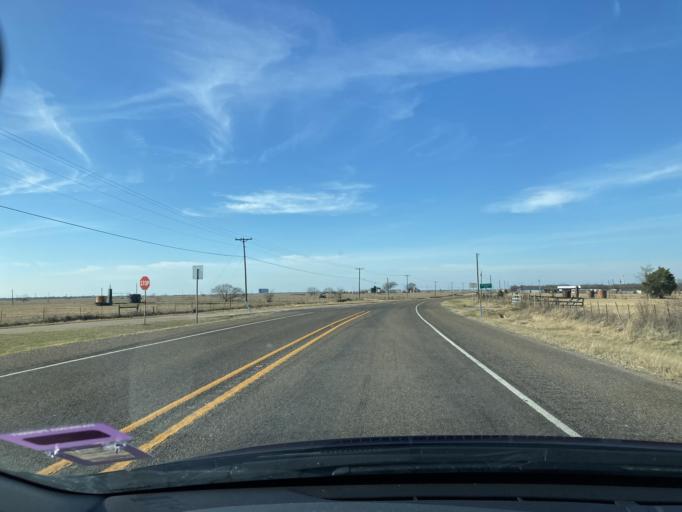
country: US
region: Texas
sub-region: Navarro County
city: Corsicana
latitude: 32.0375
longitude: -96.4048
